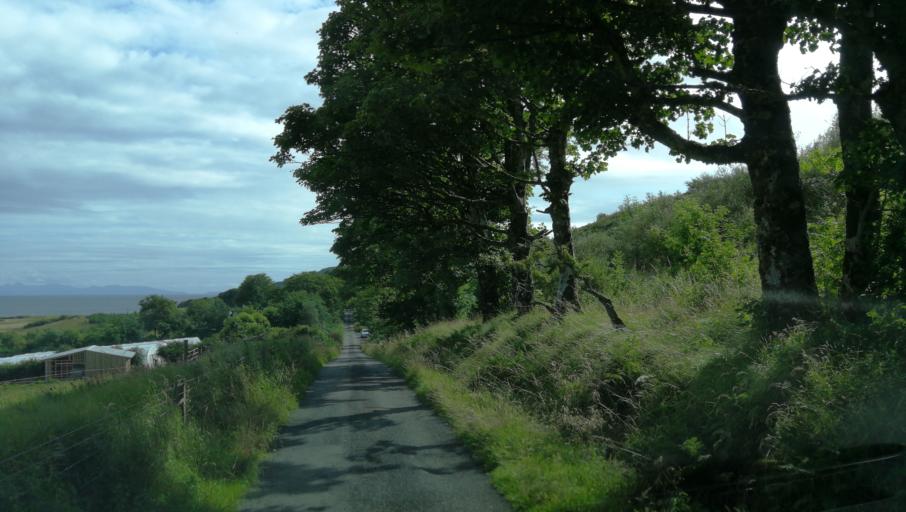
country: GB
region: Scotland
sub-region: Highland
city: Isle of Skye
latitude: 57.4013
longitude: -6.5676
